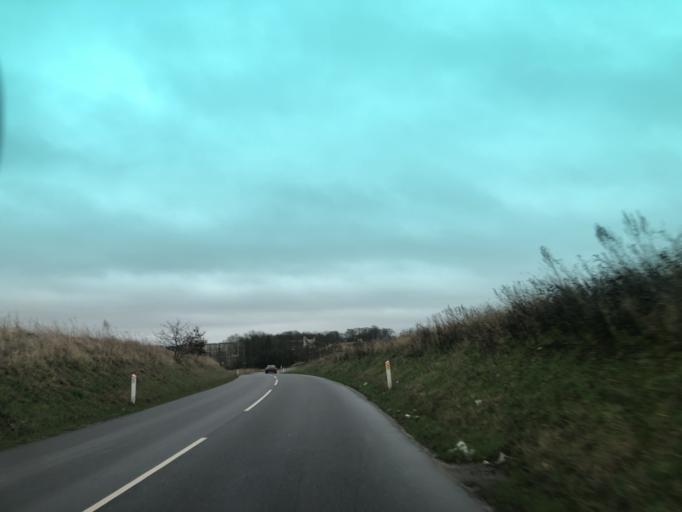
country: DK
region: Central Jutland
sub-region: Randers Kommune
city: Randers
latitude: 56.4224
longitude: 10.0672
